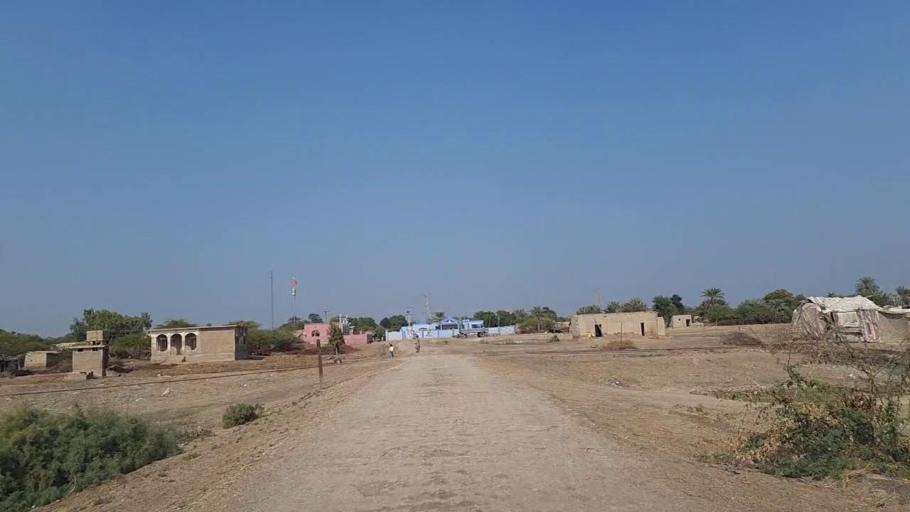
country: PK
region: Sindh
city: Jam Sahib
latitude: 26.2748
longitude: 68.5289
